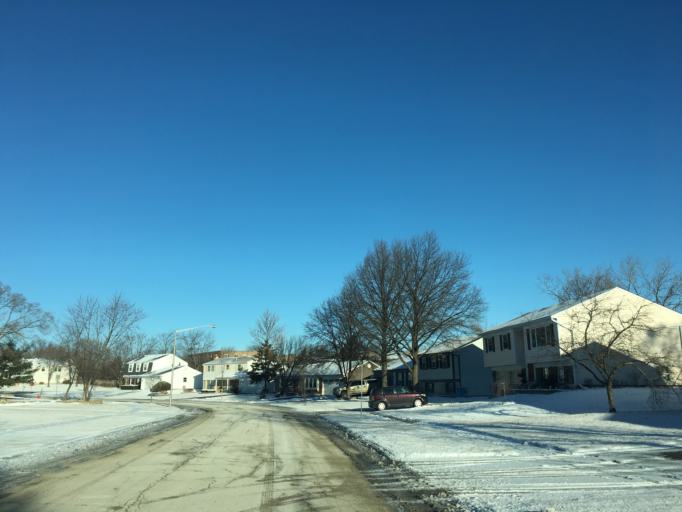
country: US
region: Illinois
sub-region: Cook County
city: Schaumburg
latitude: 42.0366
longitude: -88.1004
